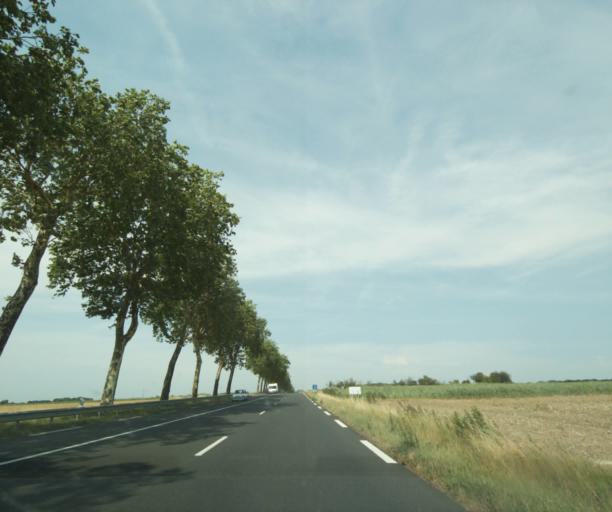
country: FR
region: Centre
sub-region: Departement d'Indre-et-Loire
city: Sainte-Maure-de-Touraine
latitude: 47.1223
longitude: 0.6246
